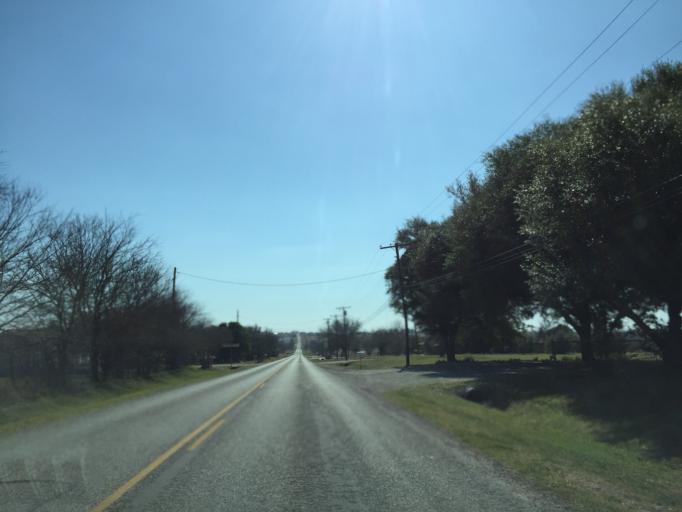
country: US
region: Texas
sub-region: Williamson County
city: Serenada
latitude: 30.7340
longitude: -97.5870
